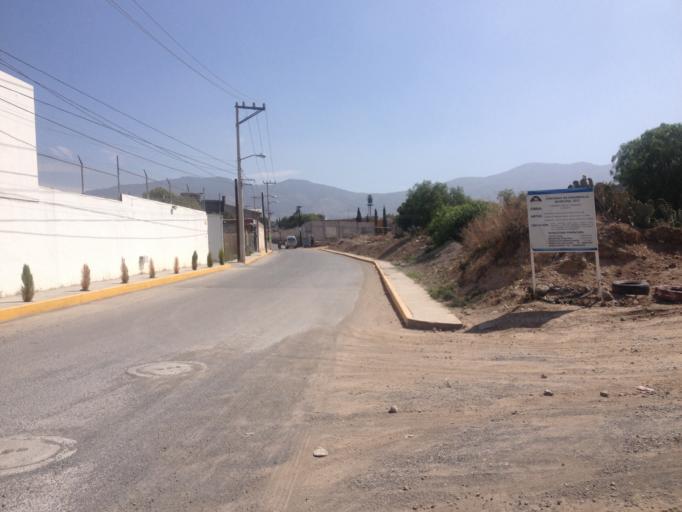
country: MX
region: Hidalgo
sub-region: Mineral de la Reforma
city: Carboneras
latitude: 20.0919
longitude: -98.7034
